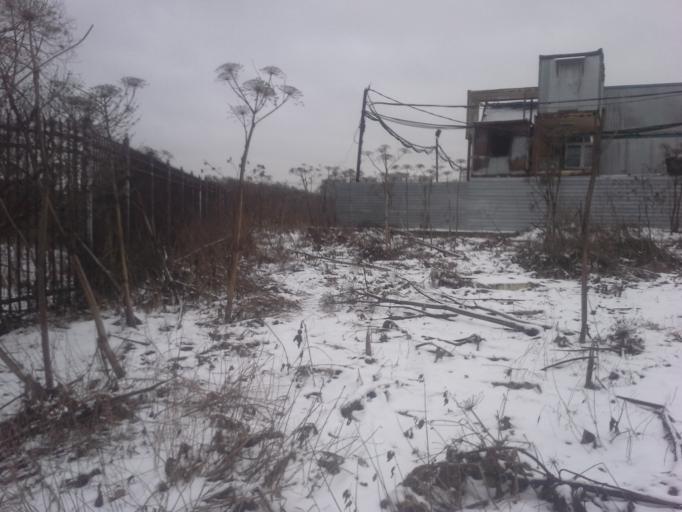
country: RU
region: Moskovskaya
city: Kommunarka
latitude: 55.5742
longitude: 37.4976
